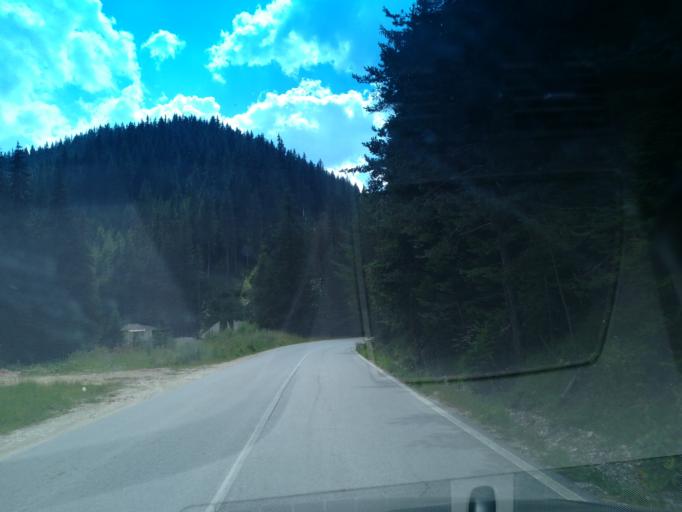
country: BG
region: Smolyan
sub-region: Obshtina Chepelare
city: Chepelare
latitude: 41.6619
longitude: 24.6568
